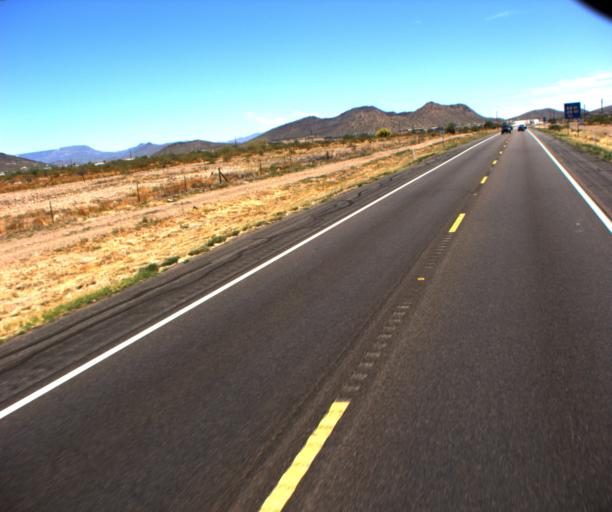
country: US
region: Arizona
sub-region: Maricopa County
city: Anthem
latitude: 33.7980
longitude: -112.1483
